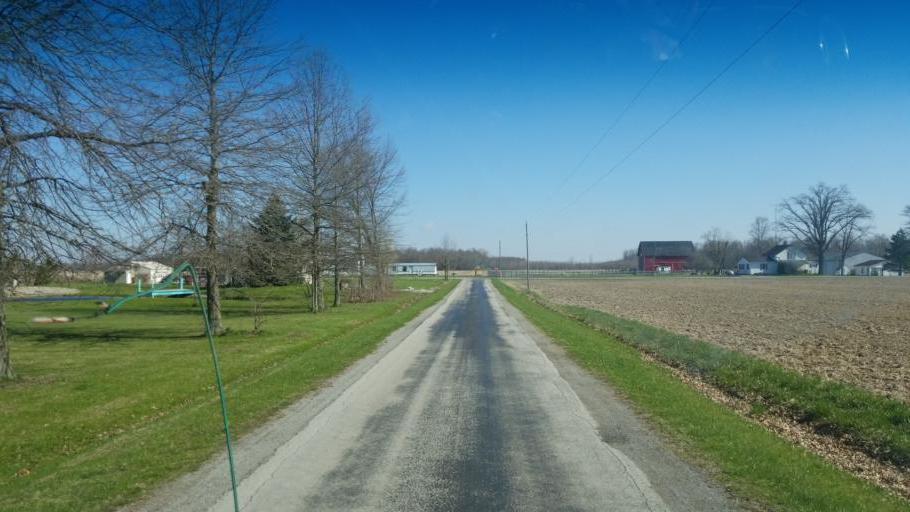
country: US
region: Ohio
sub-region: Hardin County
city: Forest
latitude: 40.7154
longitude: -83.4453
